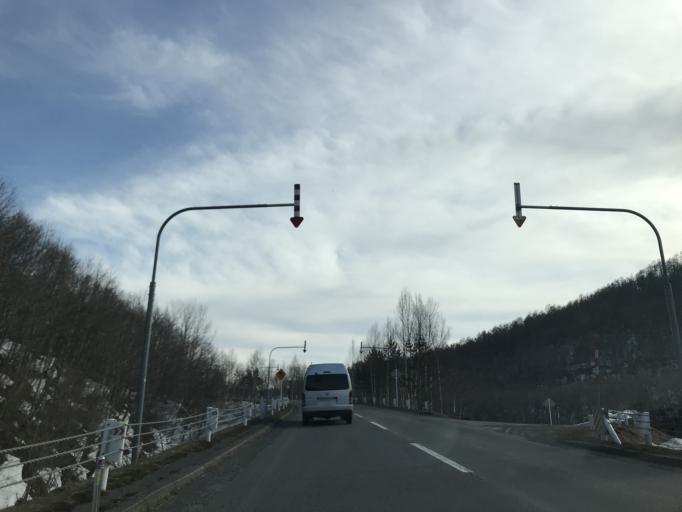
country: JP
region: Hokkaido
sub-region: Asahikawa-shi
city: Asahikawa
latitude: 43.7207
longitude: 142.3188
